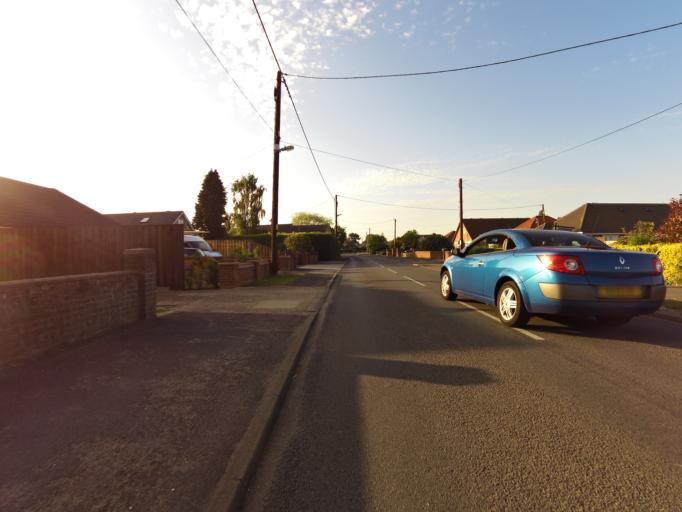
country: GB
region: England
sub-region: Suffolk
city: Kesgrave
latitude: 52.0593
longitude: 1.2335
